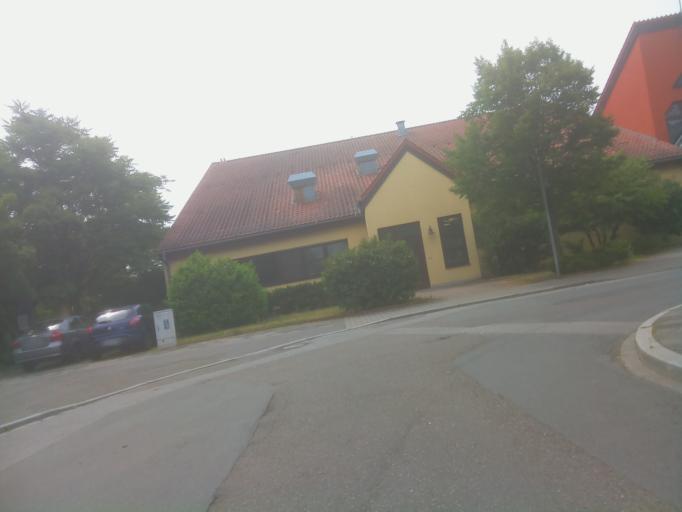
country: DE
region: Hesse
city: Lampertheim
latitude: 49.5497
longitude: 8.4731
